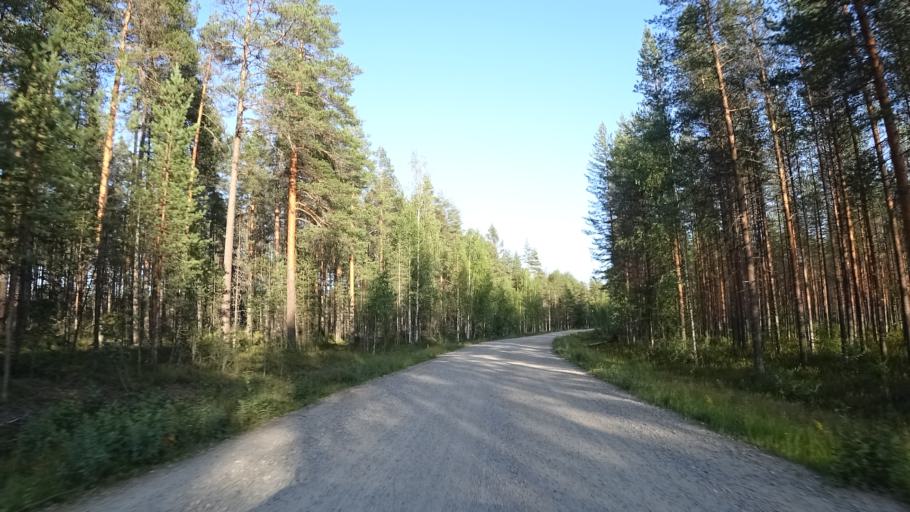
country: FI
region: North Karelia
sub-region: Joensuu
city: Ilomantsi
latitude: 63.1372
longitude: 30.7026
